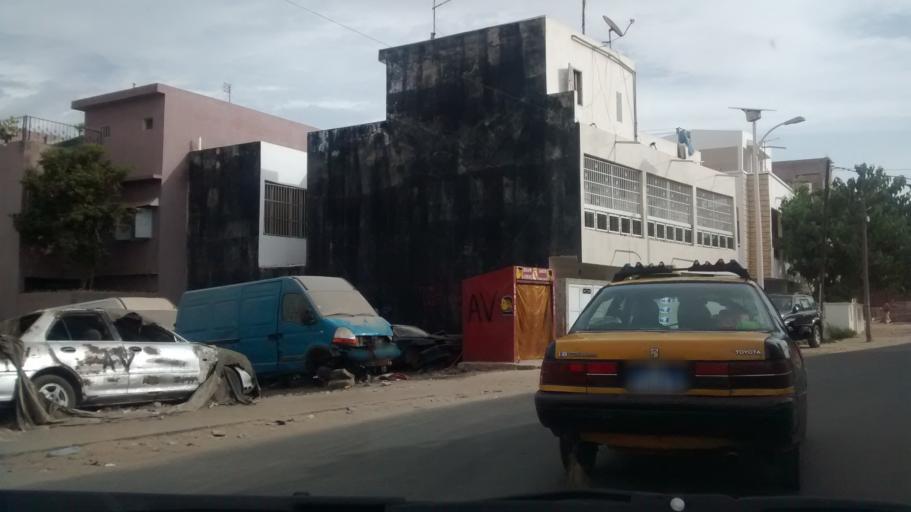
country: SN
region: Dakar
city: Pikine
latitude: 14.7609
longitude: -17.4211
